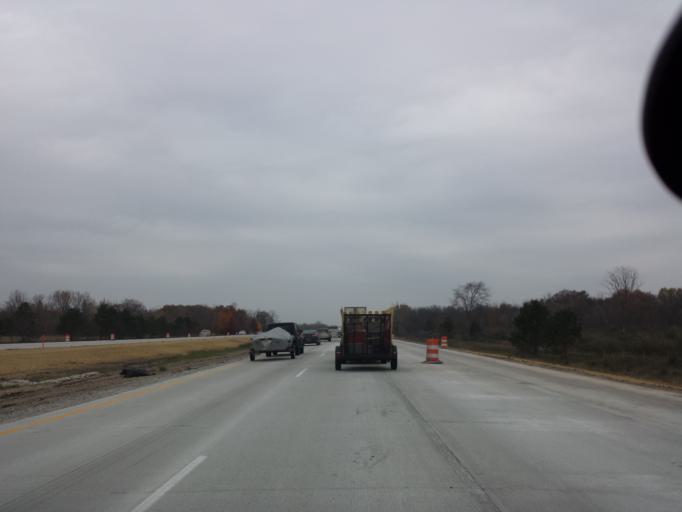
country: US
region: Michigan
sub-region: Bay County
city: Pinconning
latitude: 43.9045
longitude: -84.0200
